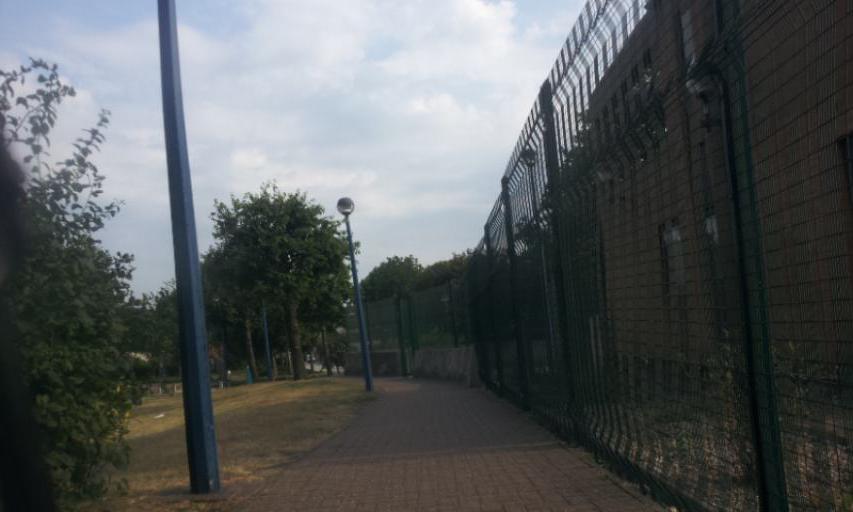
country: GB
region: England
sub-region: Greater London
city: Woolwich
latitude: 51.4947
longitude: 0.0368
